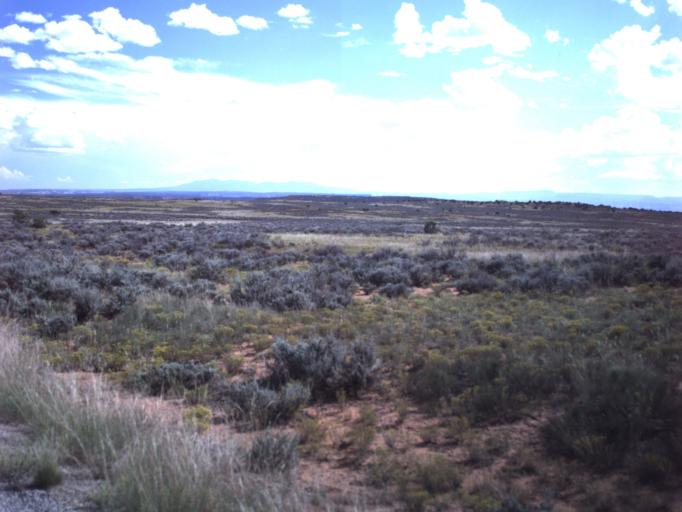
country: US
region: Utah
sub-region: Grand County
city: Moab
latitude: 38.5282
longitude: -109.7490
